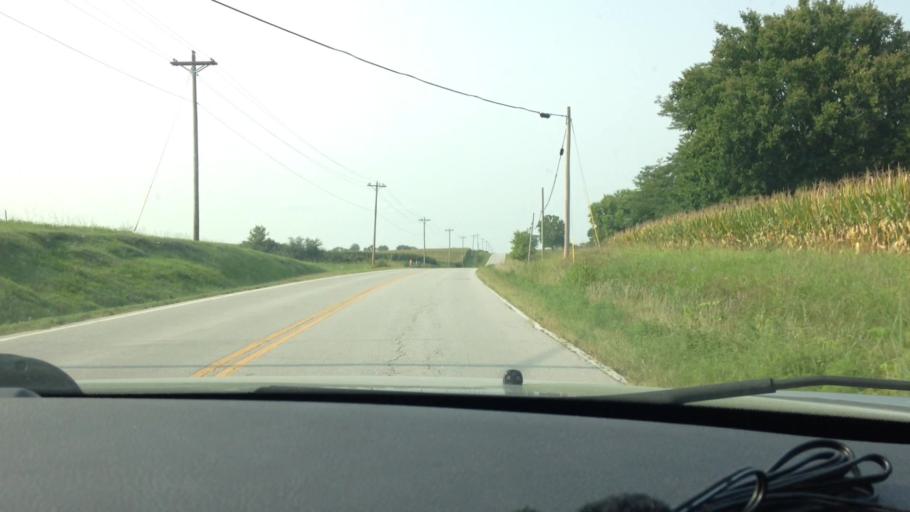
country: US
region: Missouri
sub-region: Platte County
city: Platte City
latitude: 39.4027
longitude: -94.7957
